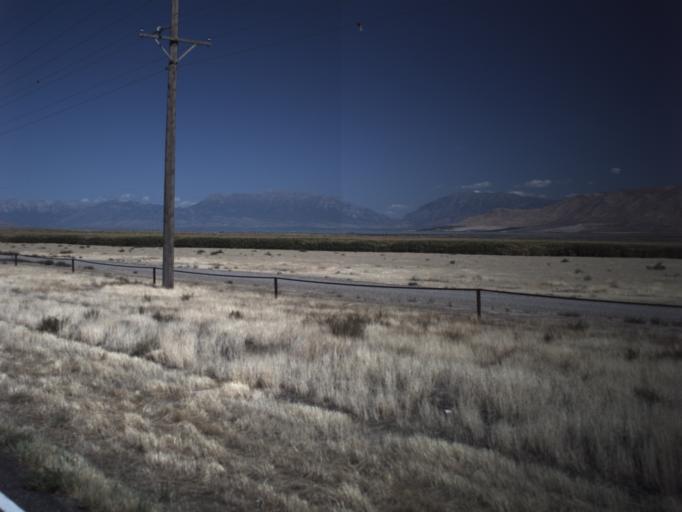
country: US
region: Utah
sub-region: Utah County
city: Genola
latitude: 40.0251
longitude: -111.9583
